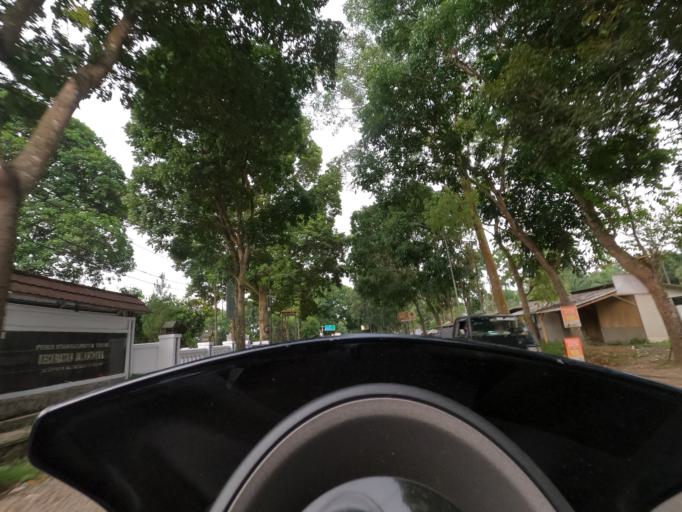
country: ID
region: West Java
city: Lembang
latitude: -6.6767
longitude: 107.6919
